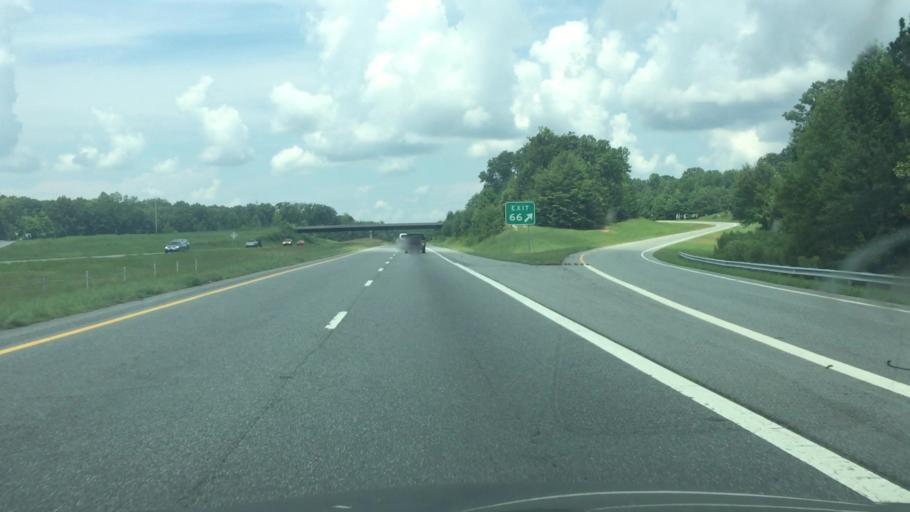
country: US
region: North Carolina
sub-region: Randolph County
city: Asheboro
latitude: 35.5897
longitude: -79.8114
